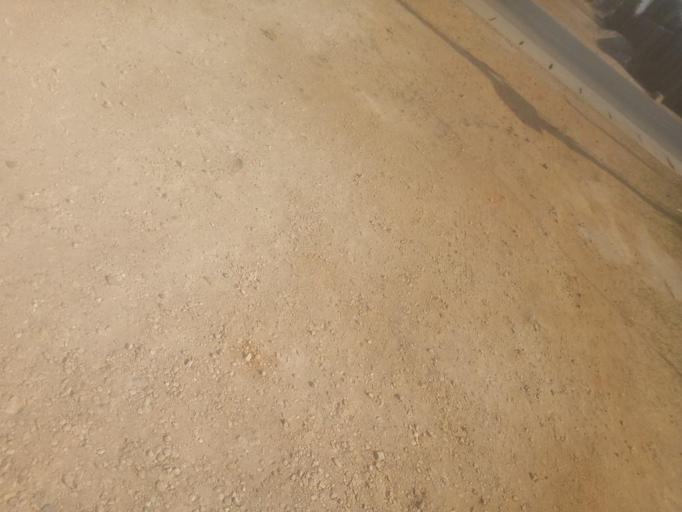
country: ZM
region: Lusaka
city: Lusaka
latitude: -15.3995
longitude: 28.3932
